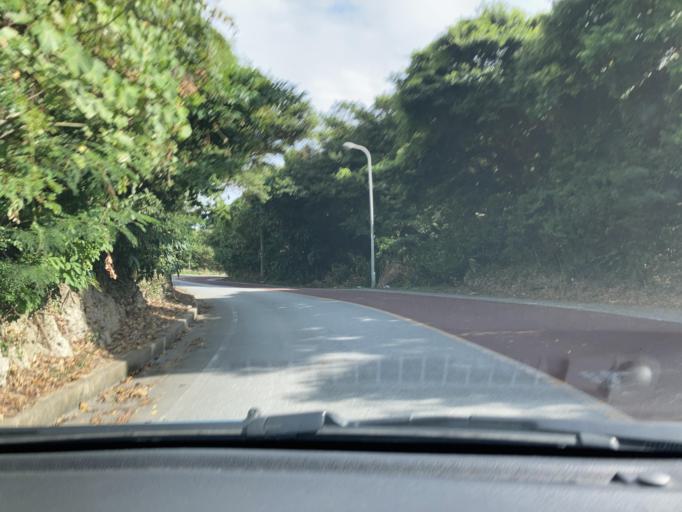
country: JP
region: Okinawa
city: Itoman
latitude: 26.0985
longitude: 127.6988
